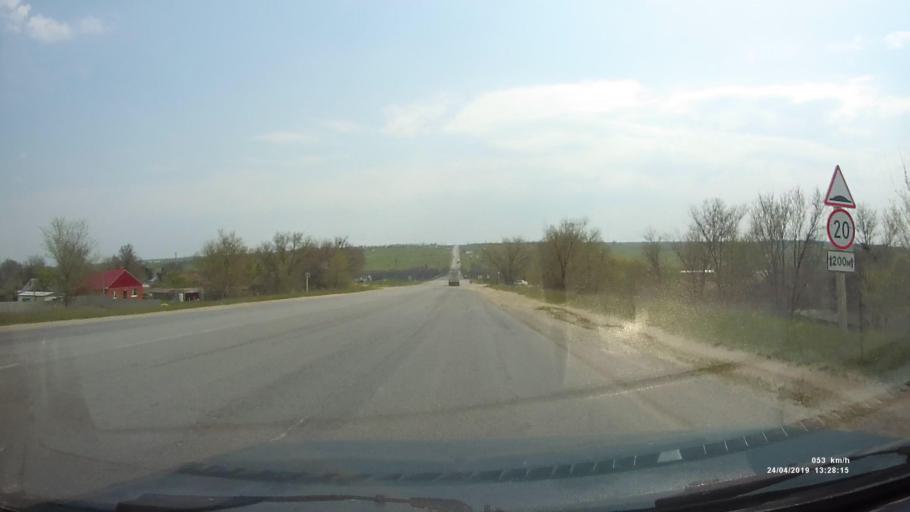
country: RU
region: Kalmykiya
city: Arshan'
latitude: 46.2743
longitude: 44.2286
